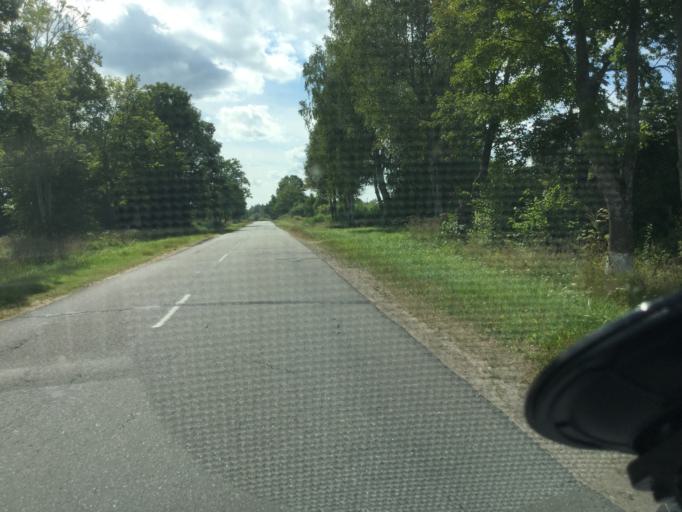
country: BY
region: Vitebsk
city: Chashniki
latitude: 55.2912
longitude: 29.3661
